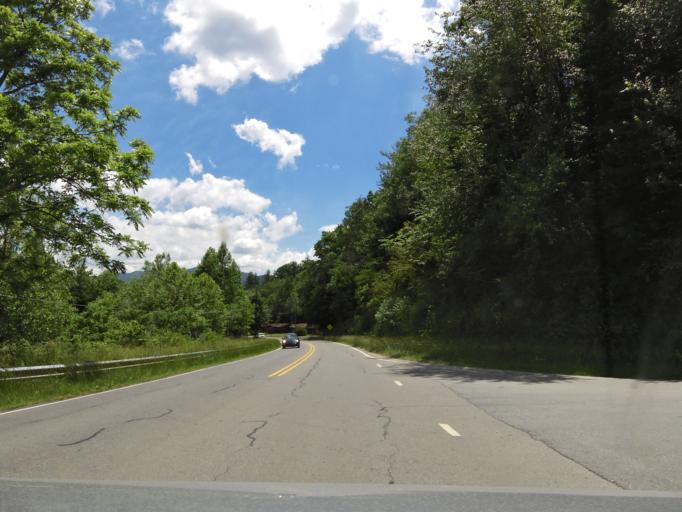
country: US
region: North Carolina
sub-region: Graham County
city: Robbinsville
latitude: 35.3325
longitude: -83.8130
